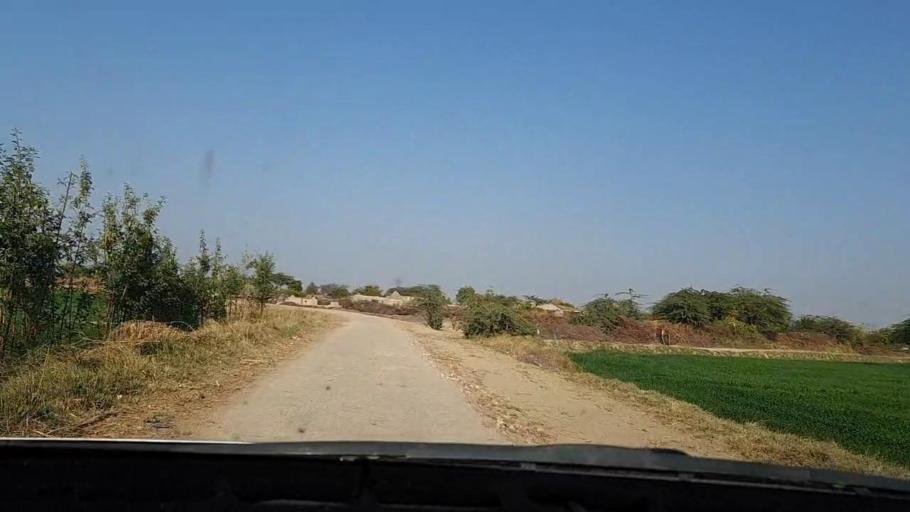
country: PK
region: Sindh
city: Tando Mittha Khan
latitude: 25.8160
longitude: 69.3157
